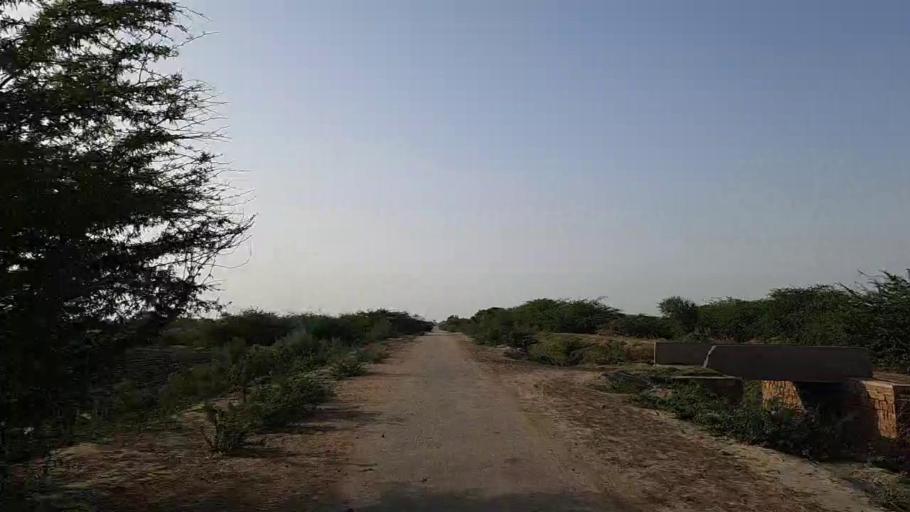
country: PK
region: Sindh
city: Jati
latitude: 24.3326
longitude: 68.1567
